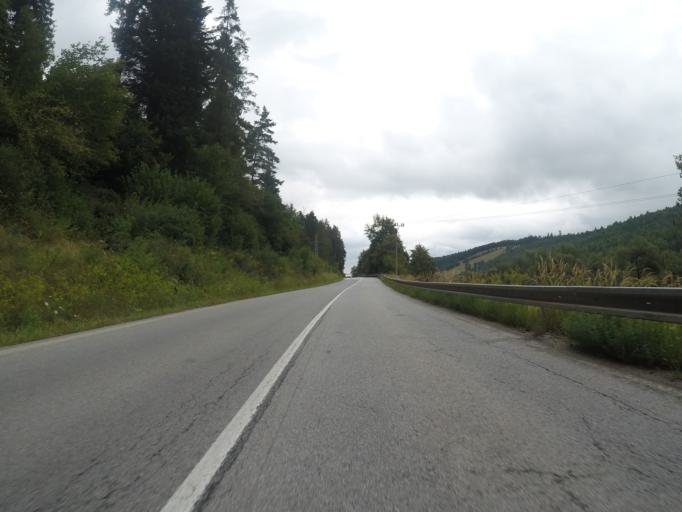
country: SK
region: Kosicky
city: Spisska Nova Ves
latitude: 48.9131
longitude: 20.5304
